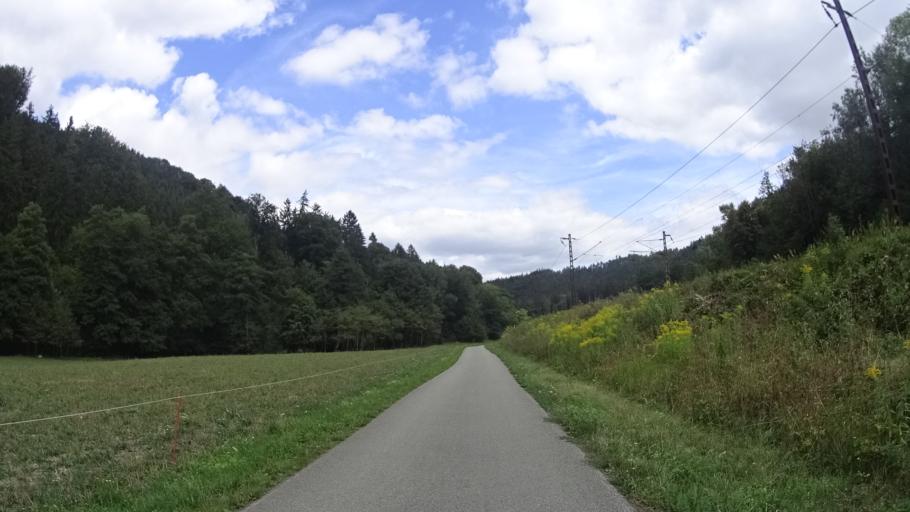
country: CZ
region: Pardubicky
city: Brandys nad Orlici
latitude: 49.9783
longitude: 16.3344
